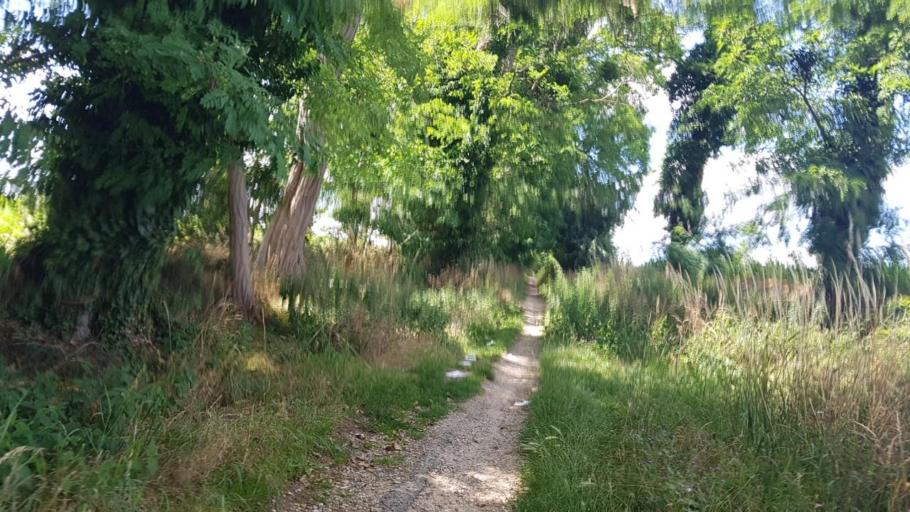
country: FR
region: Ile-de-France
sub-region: Departement de Seine-et-Marne
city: Moussy-le-Vieux
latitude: 49.0393
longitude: 2.6342
